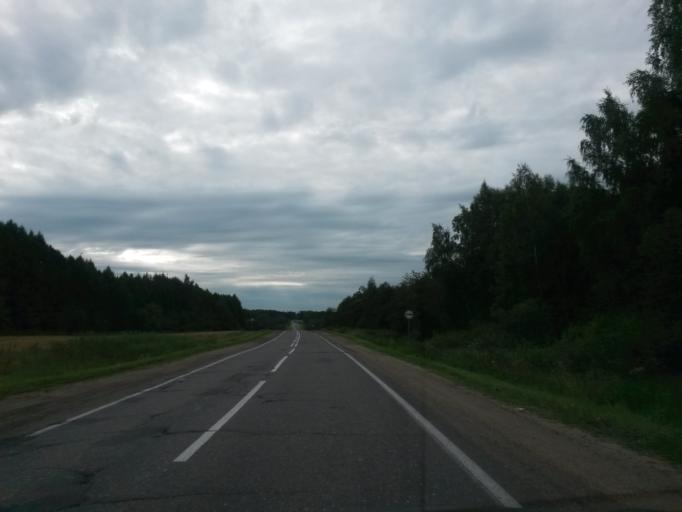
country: RU
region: Jaroslavl
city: Krasnyye Tkachi
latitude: 57.3888
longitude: 39.6890
